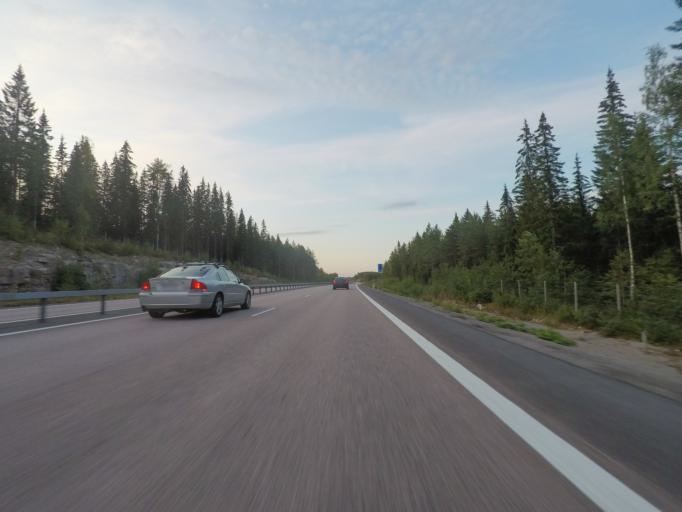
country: FI
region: Central Finland
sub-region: Jyvaeskylae
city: Saeynaetsalo
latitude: 62.1614
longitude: 25.8990
